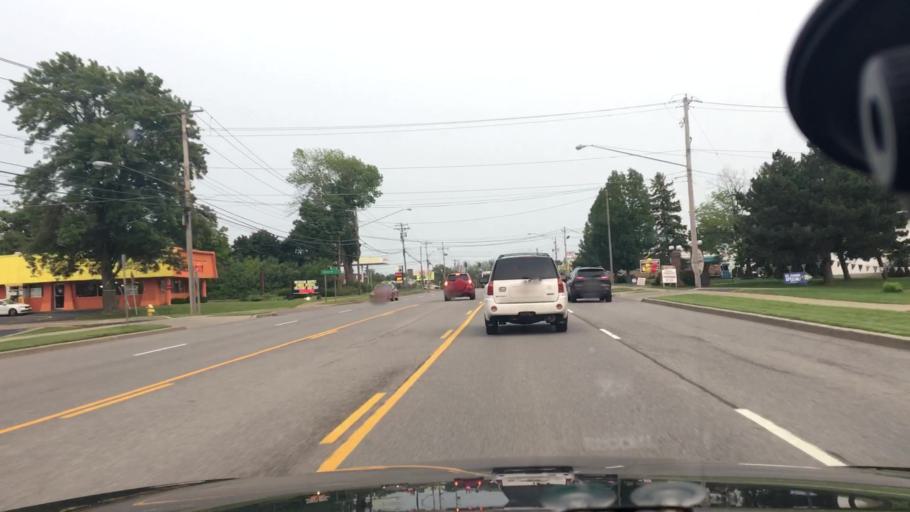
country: US
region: New York
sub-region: Erie County
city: Hamburg
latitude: 42.7356
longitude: -78.8407
